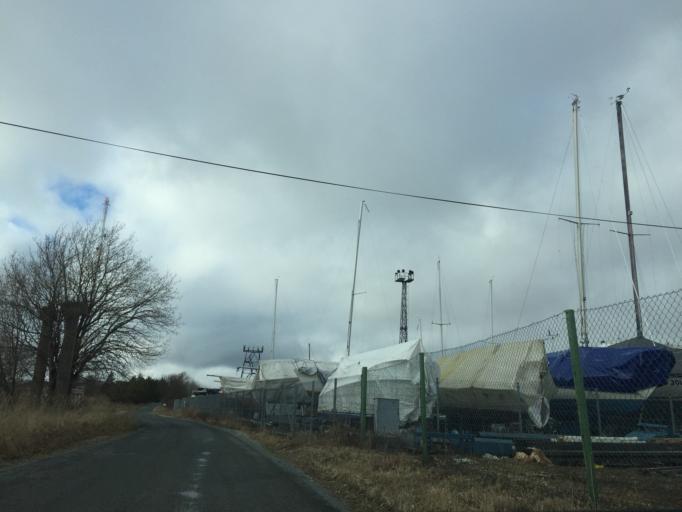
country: EE
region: Laeaene
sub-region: Haapsalu linn
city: Haapsalu
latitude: 58.9591
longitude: 23.5231
